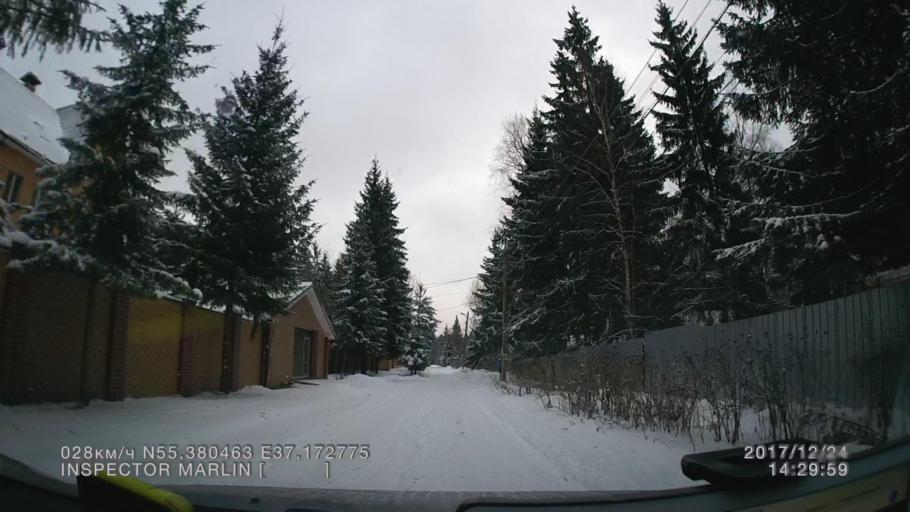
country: RU
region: Moskovskaya
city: Troitsk
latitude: 55.3804
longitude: 37.1730
